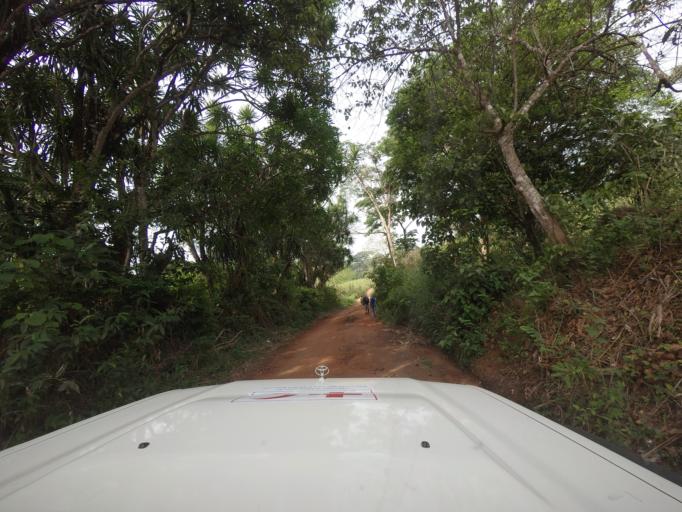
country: GN
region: Nzerekore
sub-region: Macenta
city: Macenta
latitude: 8.5303
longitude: -9.5050
